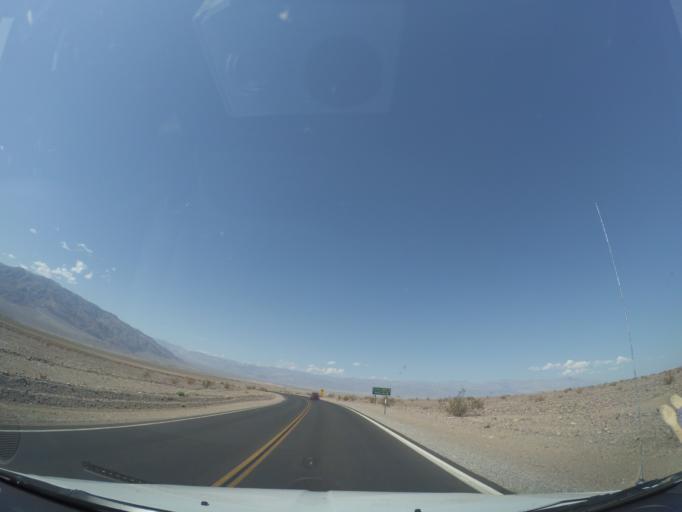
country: US
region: Nevada
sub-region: Nye County
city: Beatty
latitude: 36.6398
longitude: -117.0335
